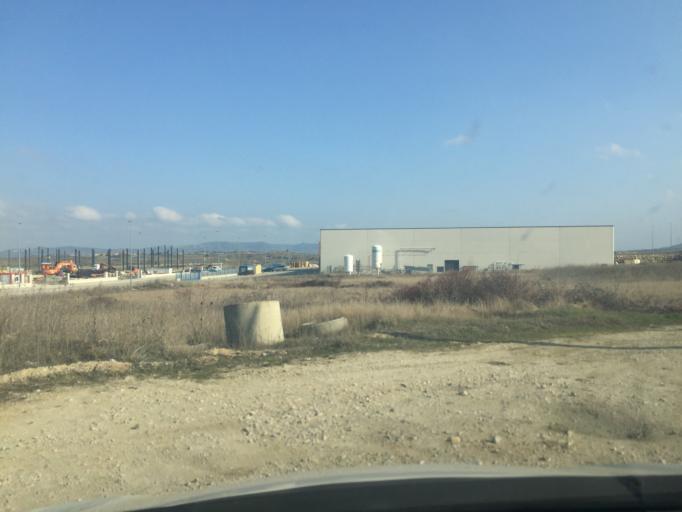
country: ES
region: Castille and Leon
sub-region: Provincia de Burgos
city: Medina de Pomar
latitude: 42.9191
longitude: -3.5813
